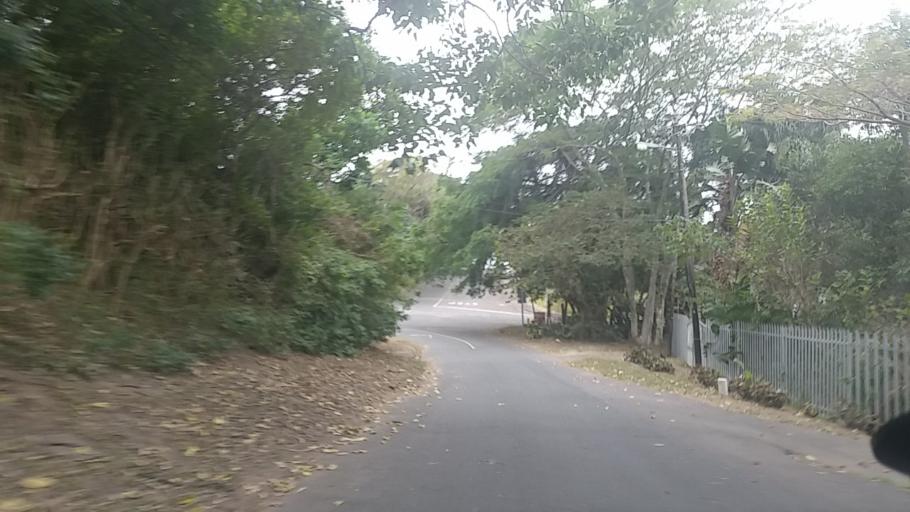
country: ZA
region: KwaZulu-Natal
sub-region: eThekwini Metropolitan Municipality
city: Berea
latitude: -29.8418
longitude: 30.9377
